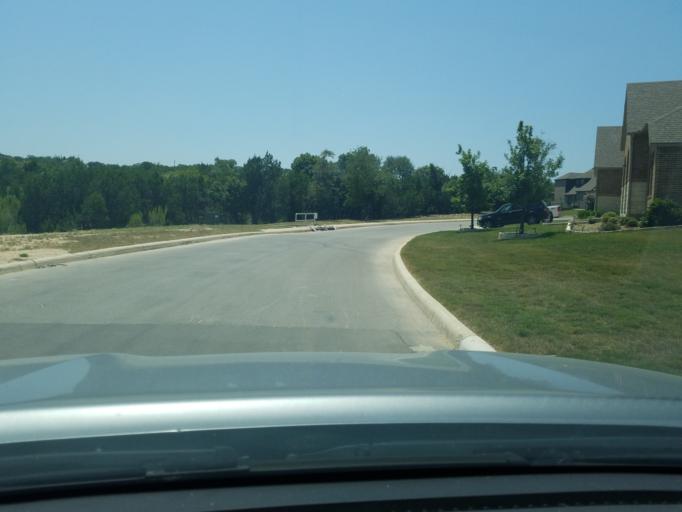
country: US
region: Texas
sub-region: Bexar County
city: Timberwood Park
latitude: 29.7122
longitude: -98.5062
